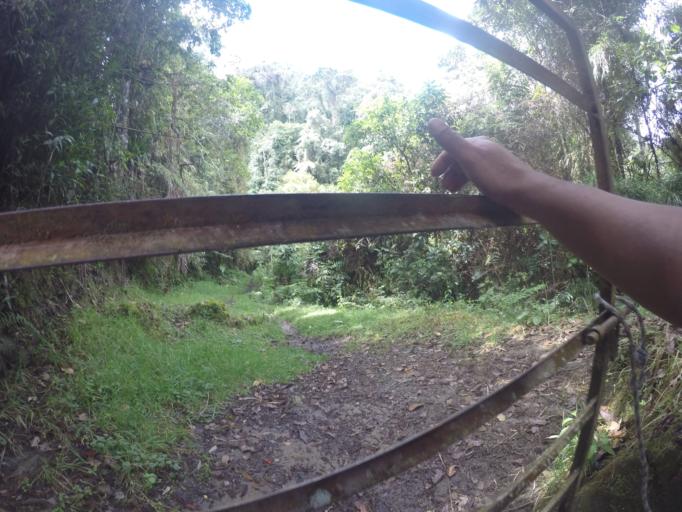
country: CO
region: Tolima
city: Cajamarca
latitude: 4.5351
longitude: -75.3479
